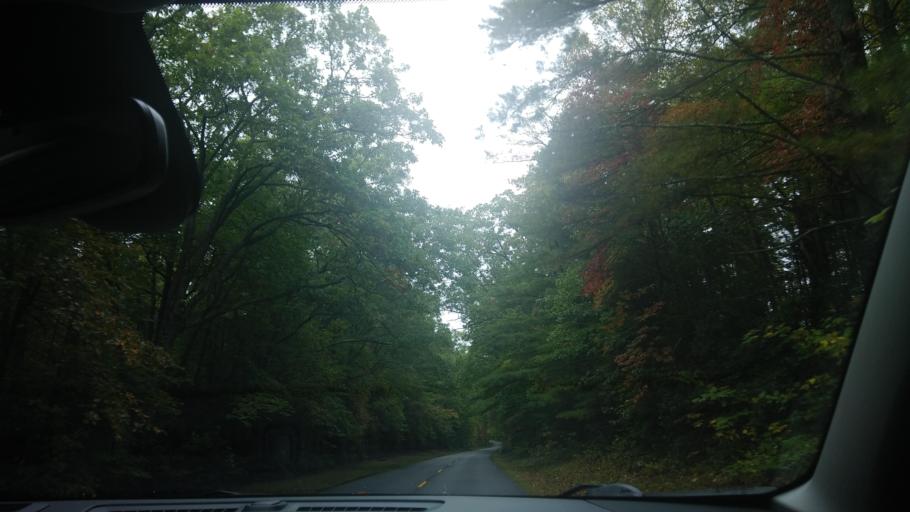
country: US
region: North Carolina
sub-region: Mitchell County
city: Spruce Pine
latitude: 35.8973
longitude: -81.9796
